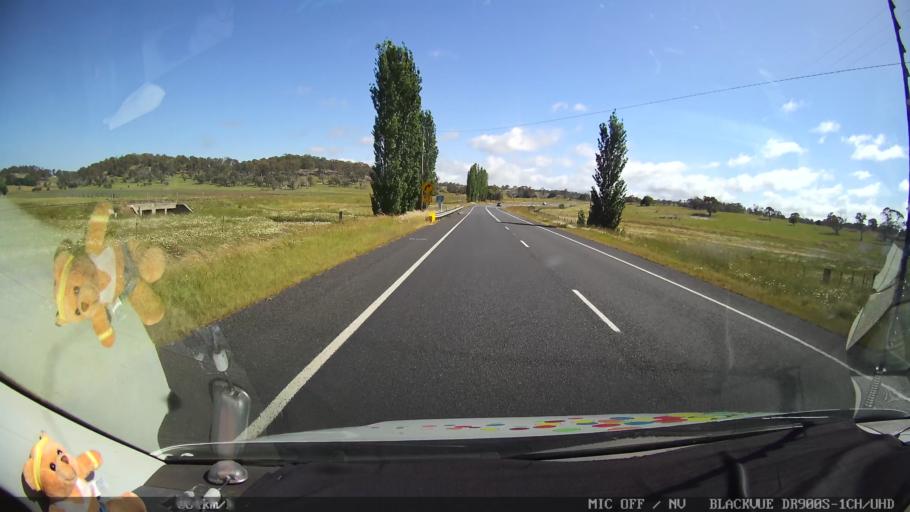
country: AU
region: New South Wales
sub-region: Guyra
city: Guyra
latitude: -30.1271
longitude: 151.6851
